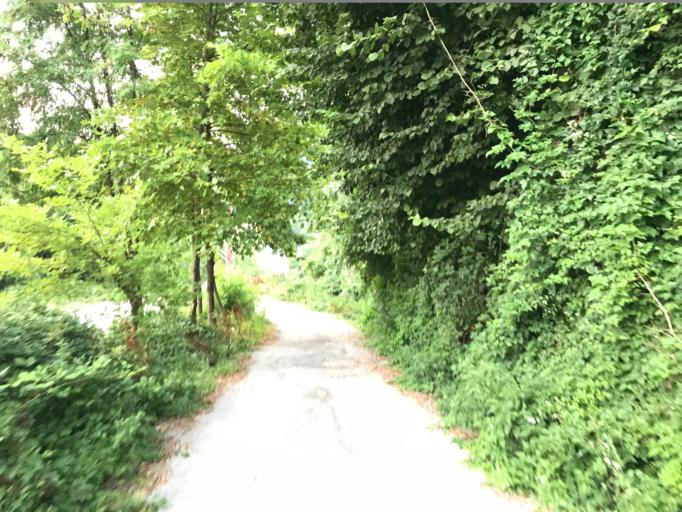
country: TR
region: Bursa
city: Tahtakopru
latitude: 39.9285
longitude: 29.5856
